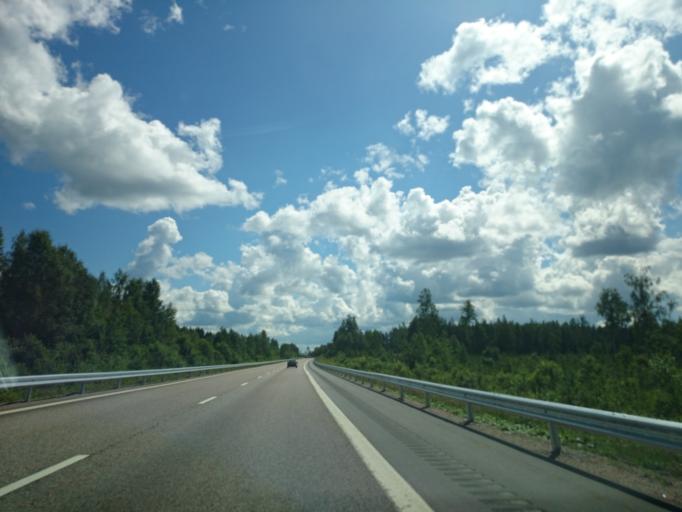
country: SE
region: Uppsala
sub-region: Alvkarleby Kommun
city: AElvkarleby
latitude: 60.4839
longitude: 17.3590
